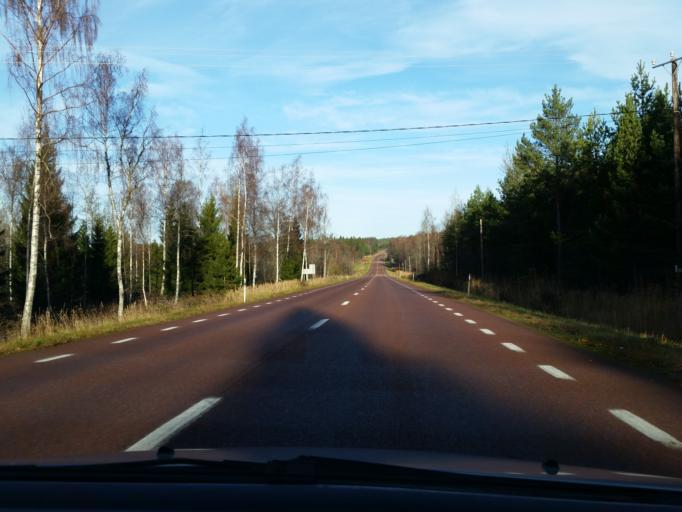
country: AX
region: Alands landsbygd
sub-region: Finstroem
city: Finstroem
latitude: 60.2943
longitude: 19.9533
